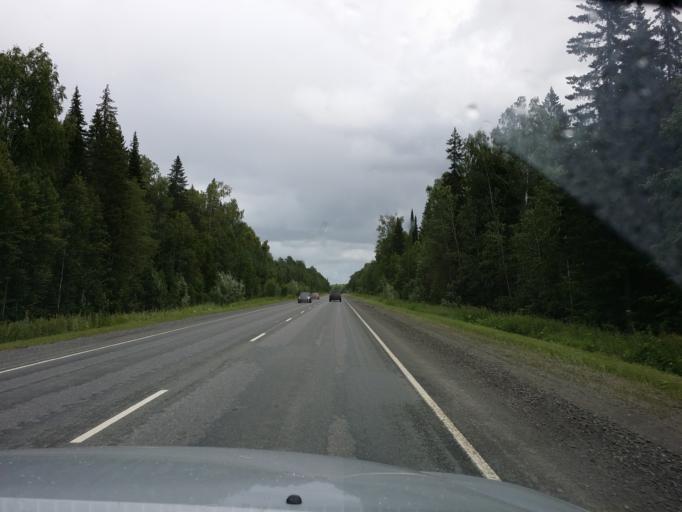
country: RU
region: Tjumen
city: Abalak
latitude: 58.4736
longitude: 68.5902
